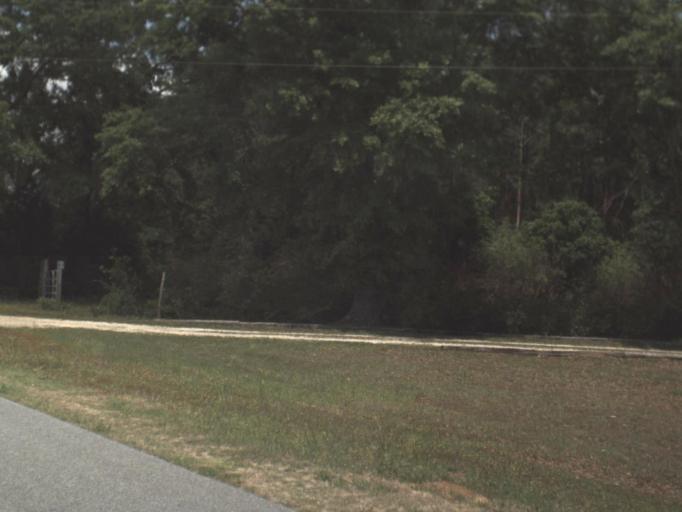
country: US
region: Alabama
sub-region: Escambia County
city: Atmore
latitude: 30.8714
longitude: -87.4424
